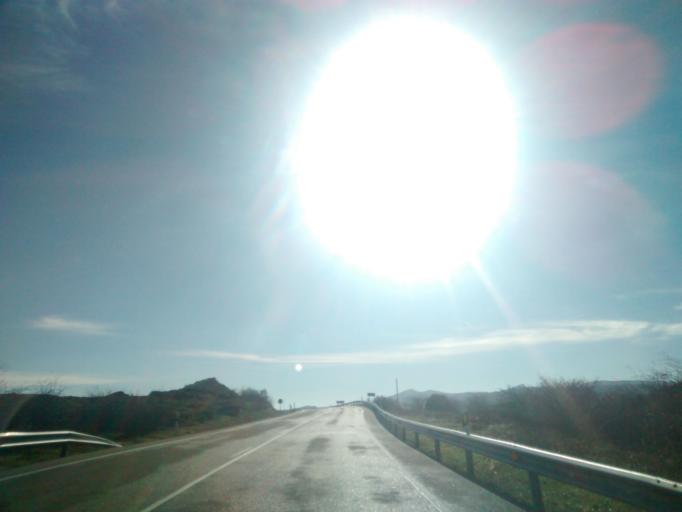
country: ES
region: Castille and Leon
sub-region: Provincia de Burgos
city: Arija
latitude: 42.9905
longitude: -3.8205
